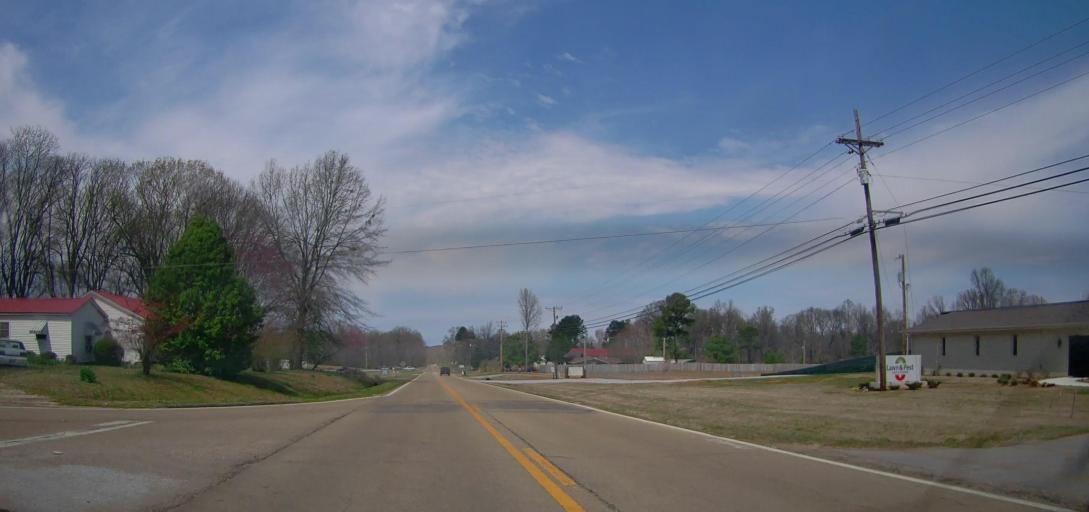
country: US
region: Mississippi
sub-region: Union County
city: New Albany
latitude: 34.4566
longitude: -88.9756
